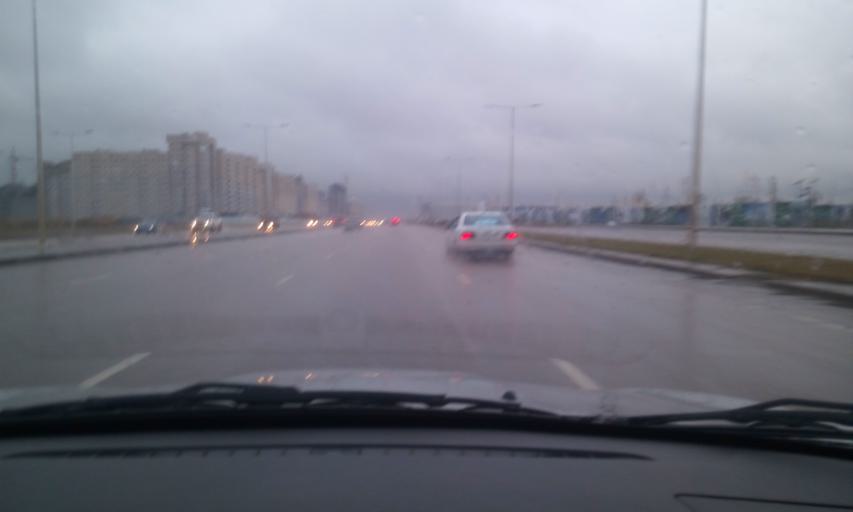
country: KZ
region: Astana Qalasy
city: Astana
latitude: 51.1294
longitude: 71.3874
